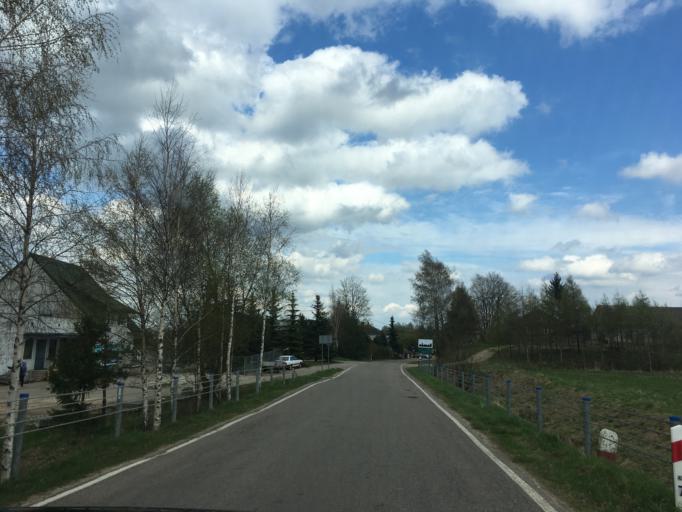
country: PL
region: Podlasie
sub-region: Suwalki
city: Suwalki
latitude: 54.3640
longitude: 22.8556
